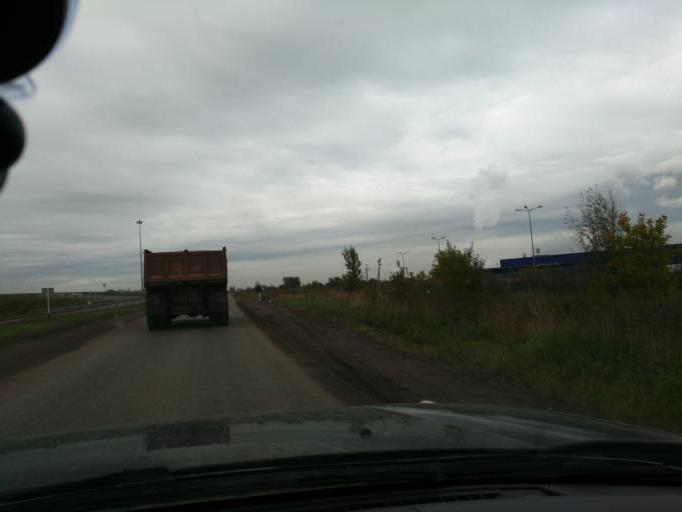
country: RU
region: Perm
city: Kondratovo
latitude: 57.9536
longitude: 56.1194
